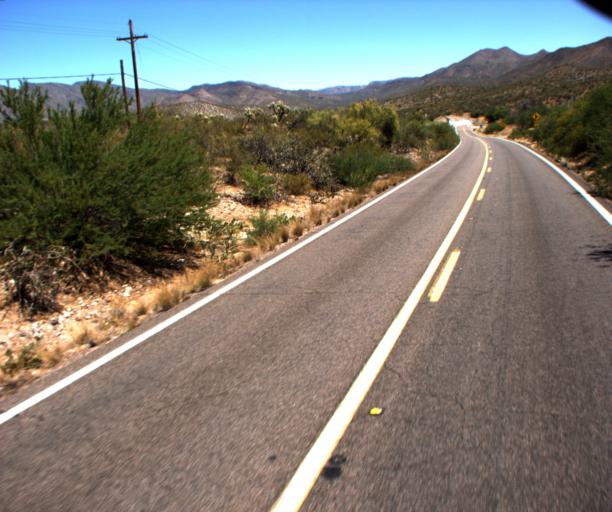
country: US
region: Arizona
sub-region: Pinal County
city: Kearny
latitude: 33.0954
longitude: -110.7299
